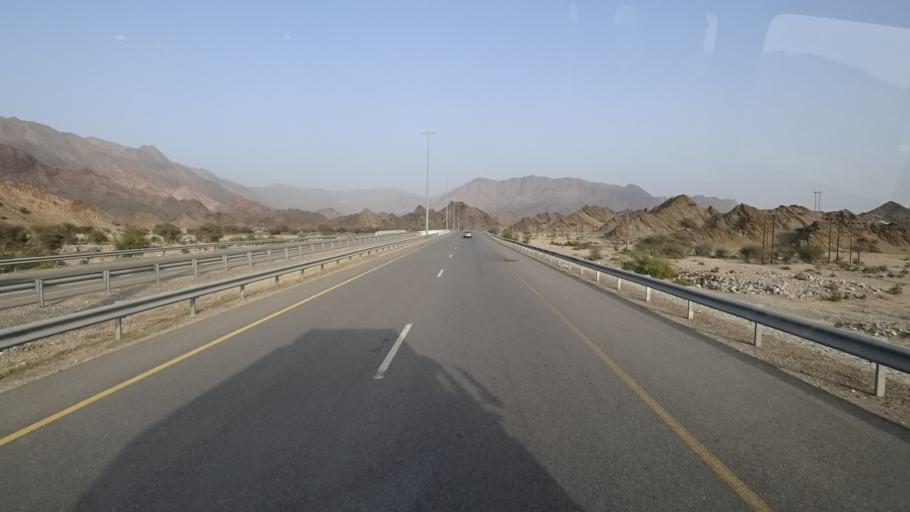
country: OM
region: Muhafazat Masqat
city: Muscat
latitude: 23.3322
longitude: 58.7081
